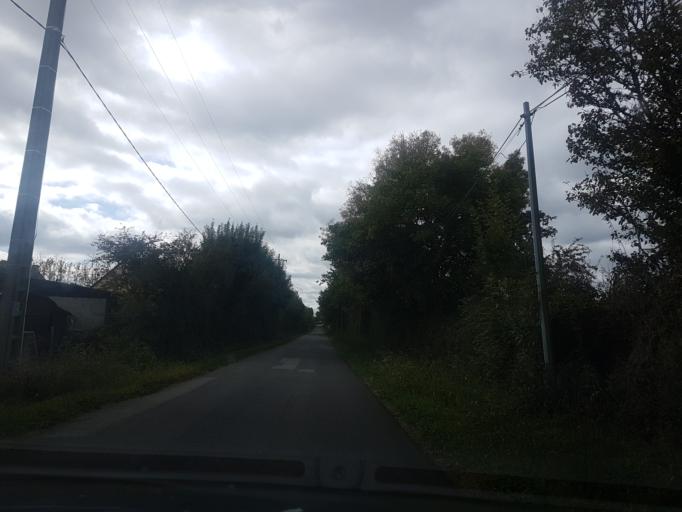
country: FR
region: Pays de la Loire
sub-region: Departement de la Loire-Atlantique
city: Ligne
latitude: 47.4095
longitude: -1.3826
